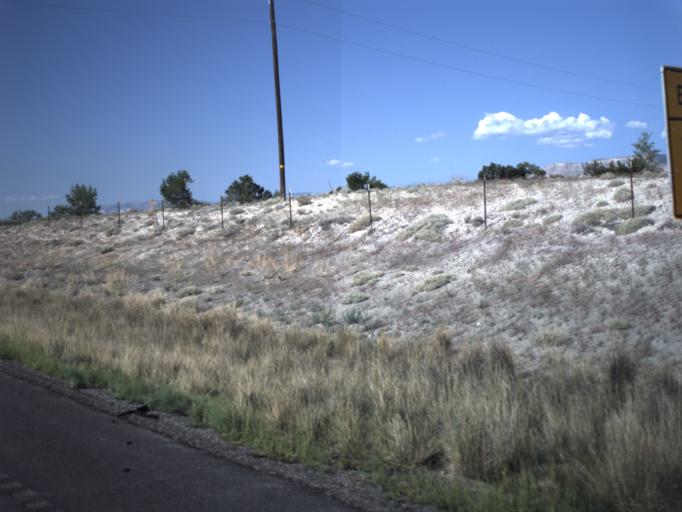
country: US
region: Utah
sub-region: Emery County
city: Castle Dale
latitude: 39.2480
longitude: -110.9875
